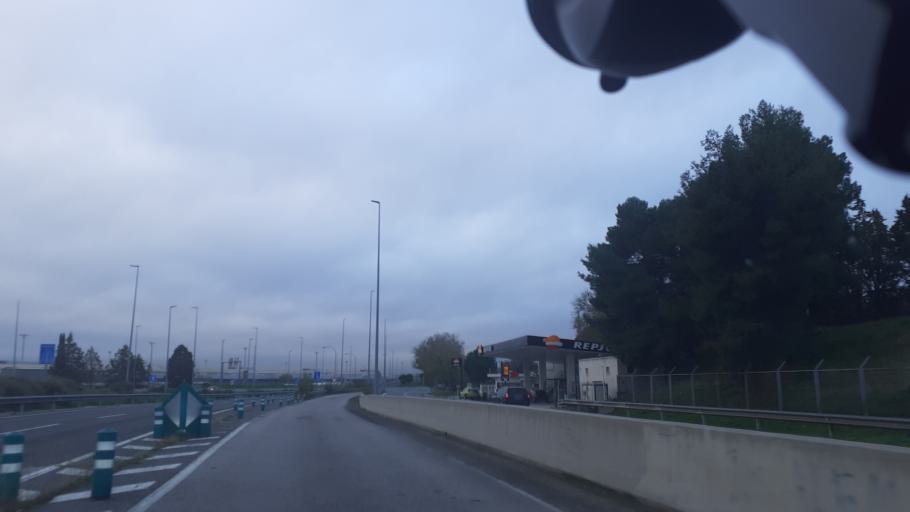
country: ES
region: Madrid
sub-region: Provincia de Madrid
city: Barajas de Madrid
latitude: 40.4649
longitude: -3.5751
